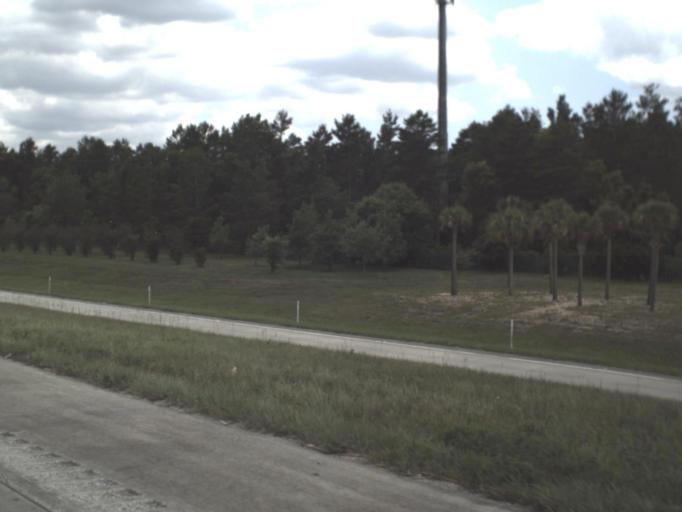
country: US
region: Florida
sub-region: Saint Johns County
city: Ponte Vedra Beach
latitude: 30.2137
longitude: -81.5142
